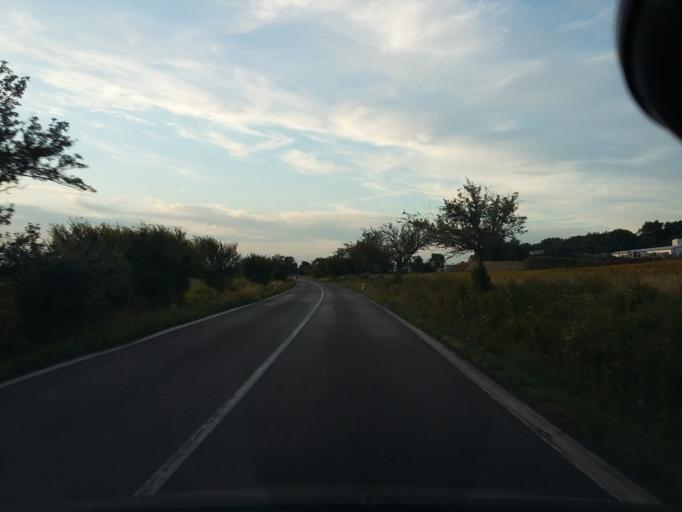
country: SK
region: Bratislavsky
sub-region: Okres Malacky
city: Malacky
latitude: 48.3977
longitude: 17.1555
